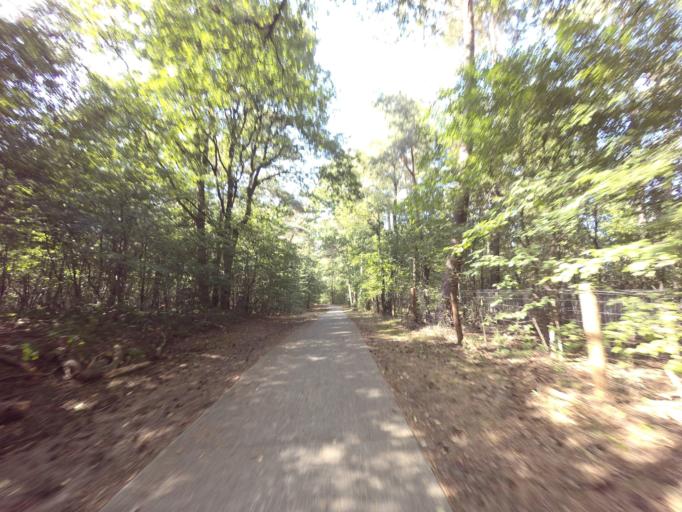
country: NL
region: Gelderland
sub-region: Gemeente Apeldoorn
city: Loenen
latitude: 52.1465
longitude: 6.0303
